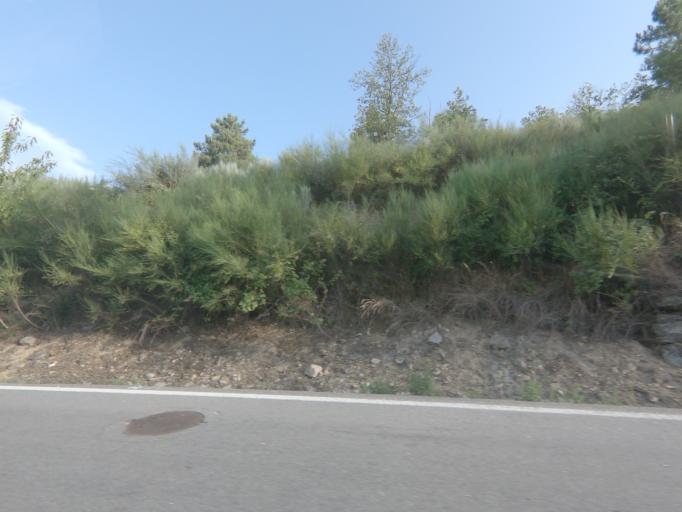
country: PT
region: Viseu
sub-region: Tabuaco
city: Tabuaco
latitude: 41.1183
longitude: -7.5831
